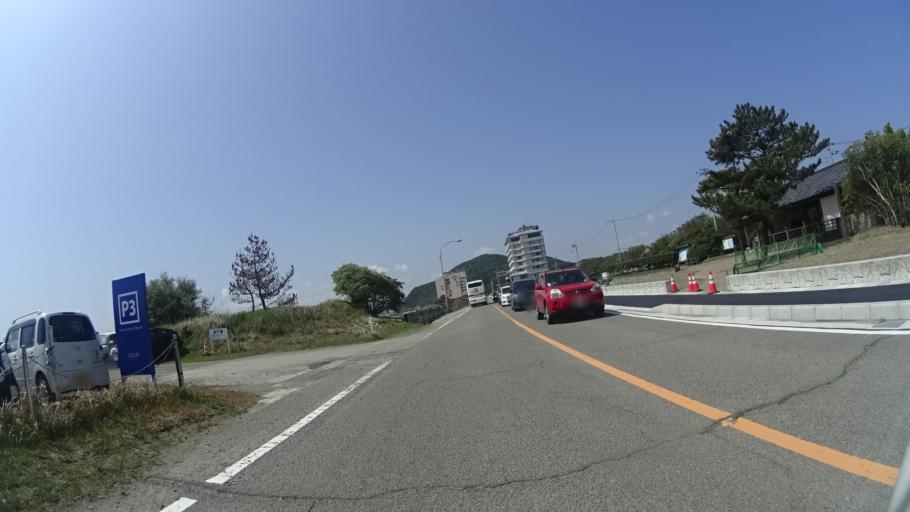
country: JP
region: Tokushima
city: Narutocho-mitsuishi
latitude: 34.2243
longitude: 134.6366
